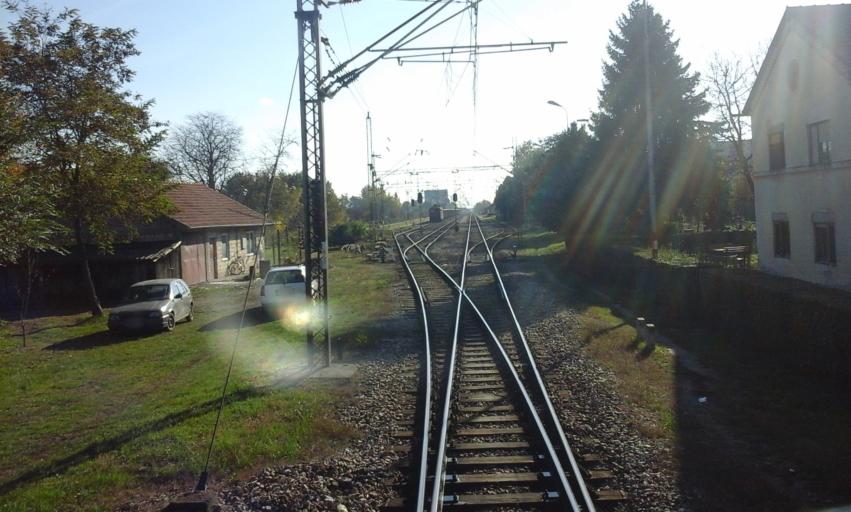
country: RS
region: Autonomna Pokrajina Vojvodina
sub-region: Severnobacki Okrug
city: Backa Topola
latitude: 45.8199
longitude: 19.6499
